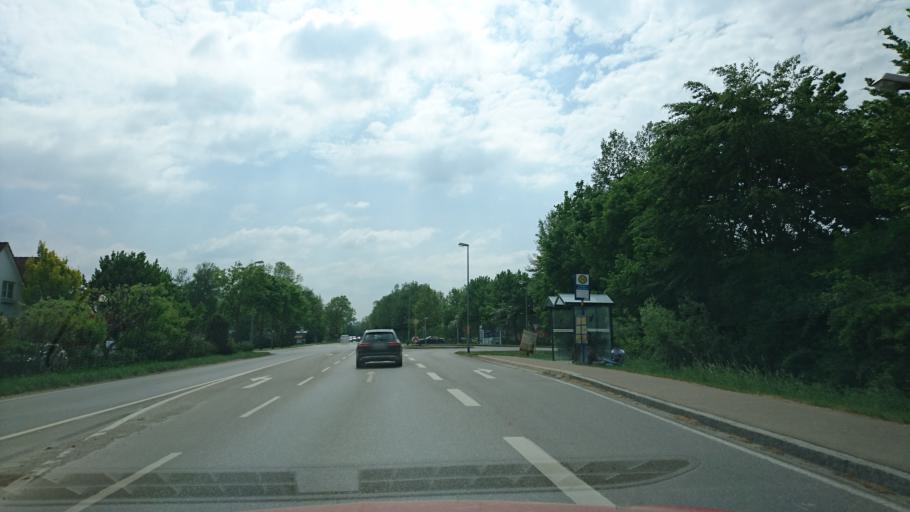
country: DE
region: Bavaria
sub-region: Swabia
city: Rehling
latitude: 48.4385
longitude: 10.9297
